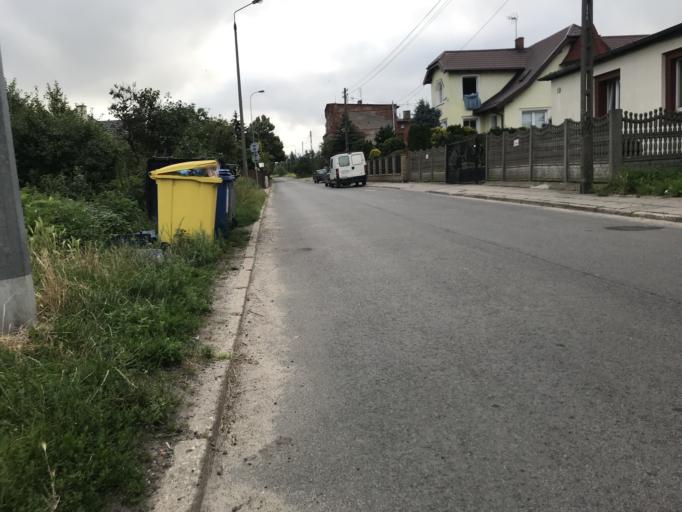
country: PL
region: Pomeranian Voivodeship
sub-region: Gdansk
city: Gdansk
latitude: 54.3362
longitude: 18.6778
